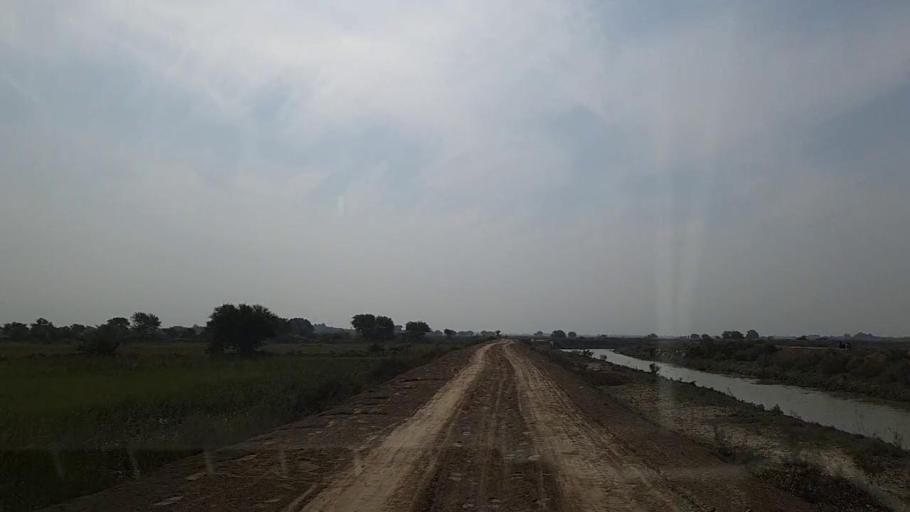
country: PK
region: Sindh
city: Mirpur Batoro
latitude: 24.6636
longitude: 68.2505
